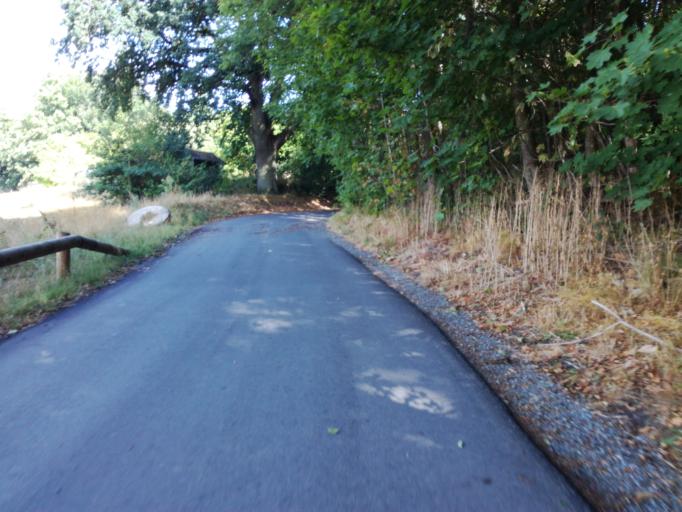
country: DK
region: South Denmark
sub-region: Vejle Kommune
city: Borkop
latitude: 55.6337
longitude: 9.6649
